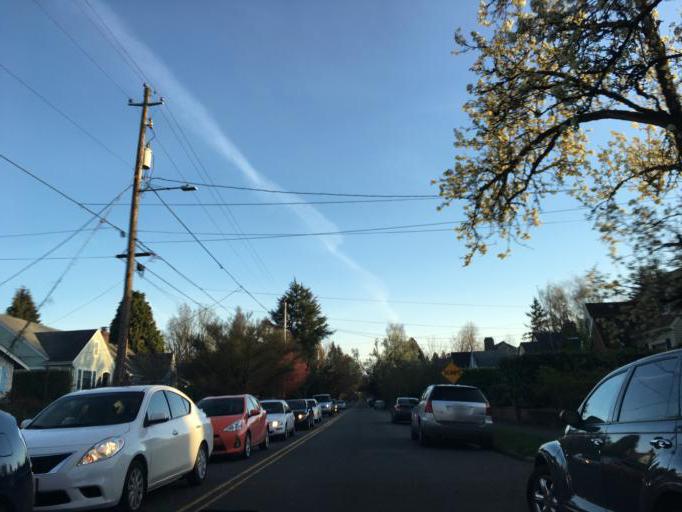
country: US
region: Oregon
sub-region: Multnomah County
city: Portland
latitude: 45.5481
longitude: -122.6504
